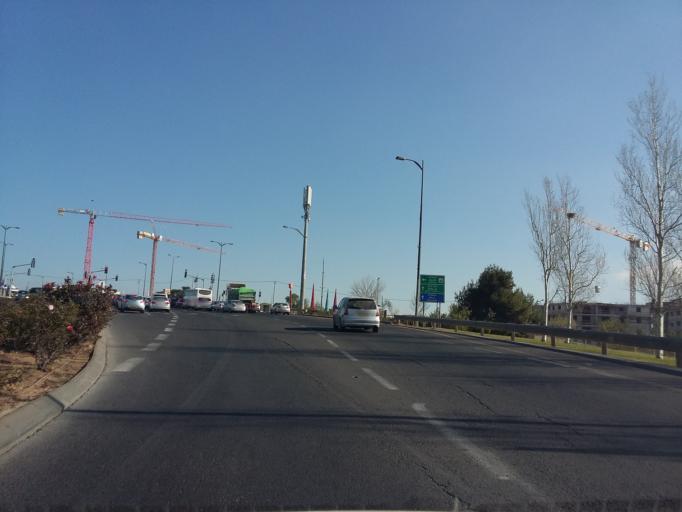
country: PS
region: West Bank
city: Ar Ram wa Dahiyat al Barid
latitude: 31.8259
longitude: 35.2361
